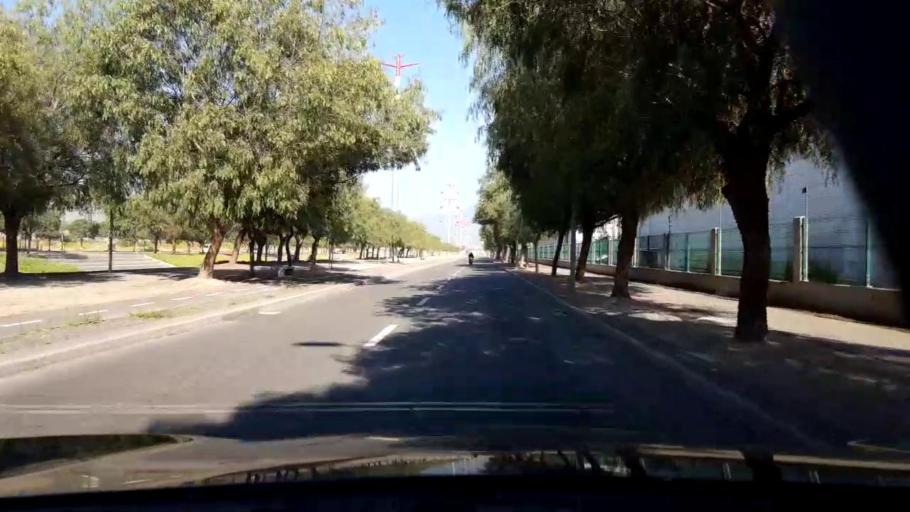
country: CL
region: Santiago Metropolitan
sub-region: Provincia de Santiago
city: Lo Prado
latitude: -33.4315
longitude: -70.7968
